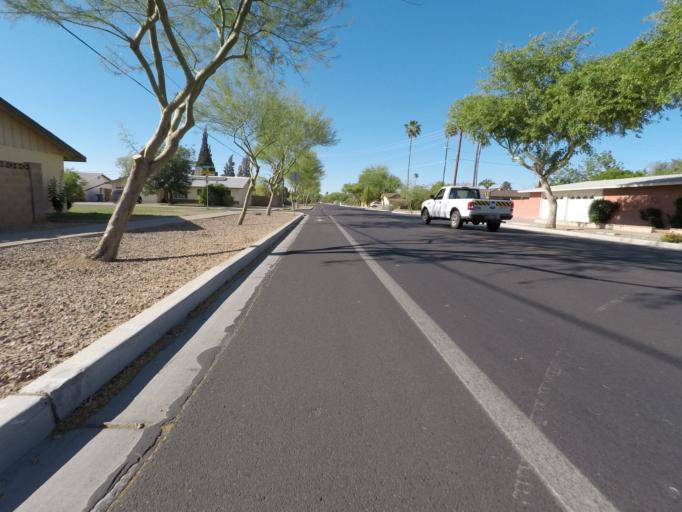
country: US
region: Arizona
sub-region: Maricopa County
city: Tempe Junction
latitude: 33.3955
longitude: -111.9350
